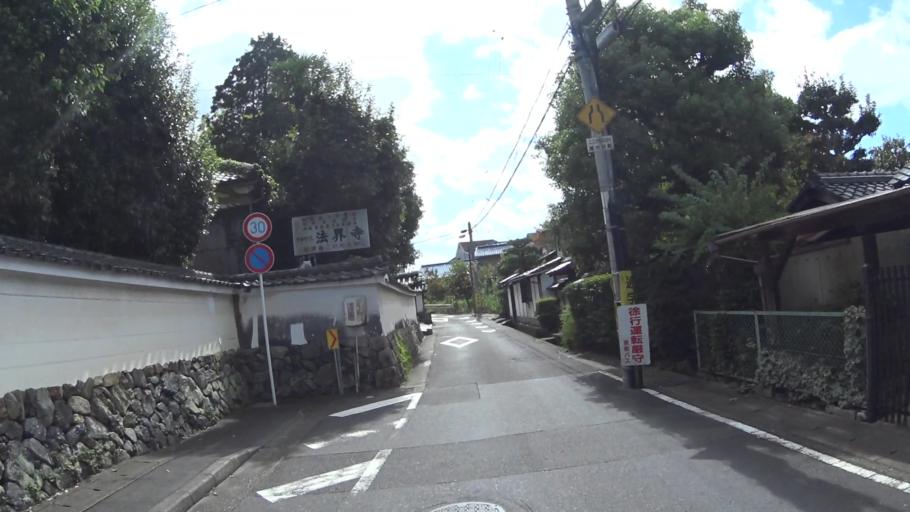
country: JP
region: Kyoto
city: Uji
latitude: 34.9345
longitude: 135.8143
